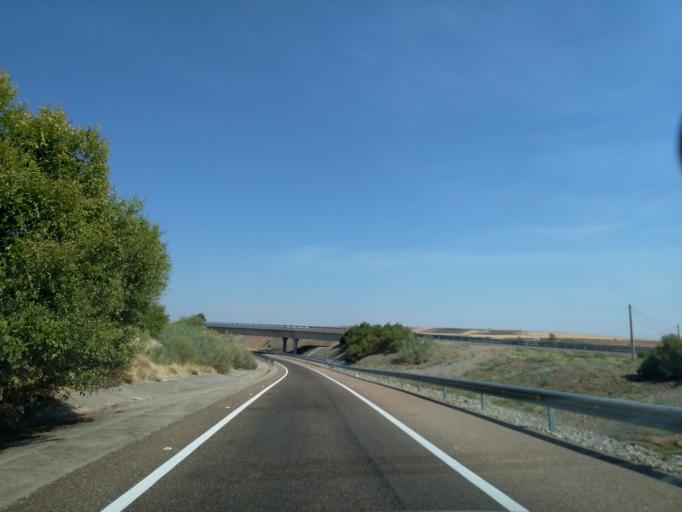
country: ES
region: Extremadura
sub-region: Provincia de Badajoz
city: Merida
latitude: 38.9457
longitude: -6.3415
